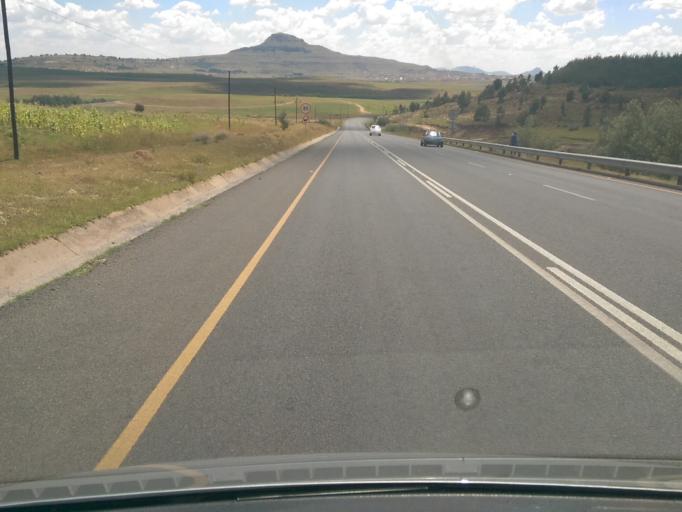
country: LS
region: Maseru
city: Maseru
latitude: -29.3951
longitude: 27.5093
